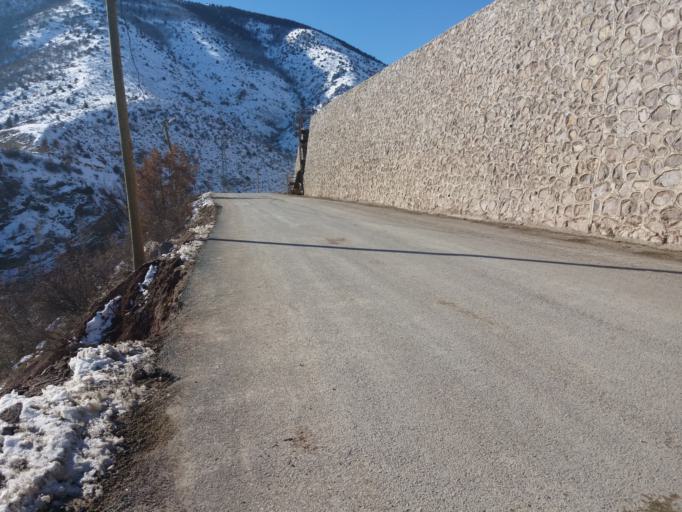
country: TR
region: Gumushane
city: Gumushkhane
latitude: 40.4405
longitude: 39.5011
